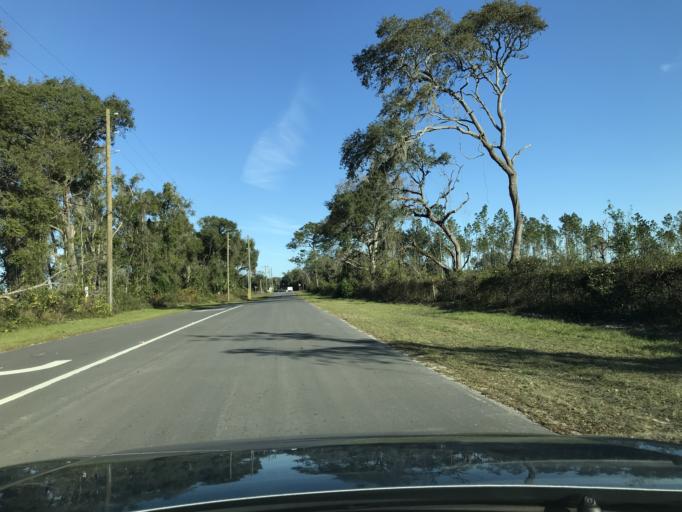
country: US
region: Florida
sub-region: Sumter County
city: Lake Panasoffkee
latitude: 28.7505
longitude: -82.0976
